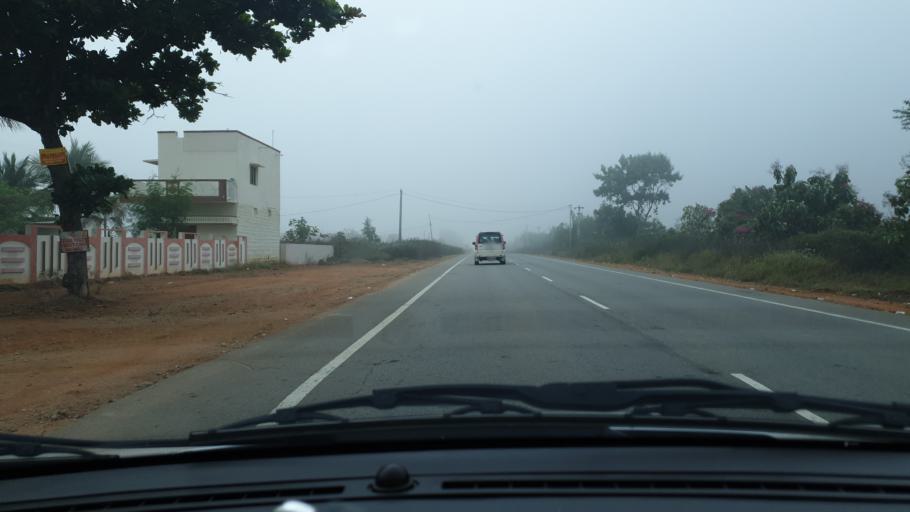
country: IN
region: Telangana
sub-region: Nalgonda
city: Devarkonda
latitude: 16.6005
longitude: 78.6805
